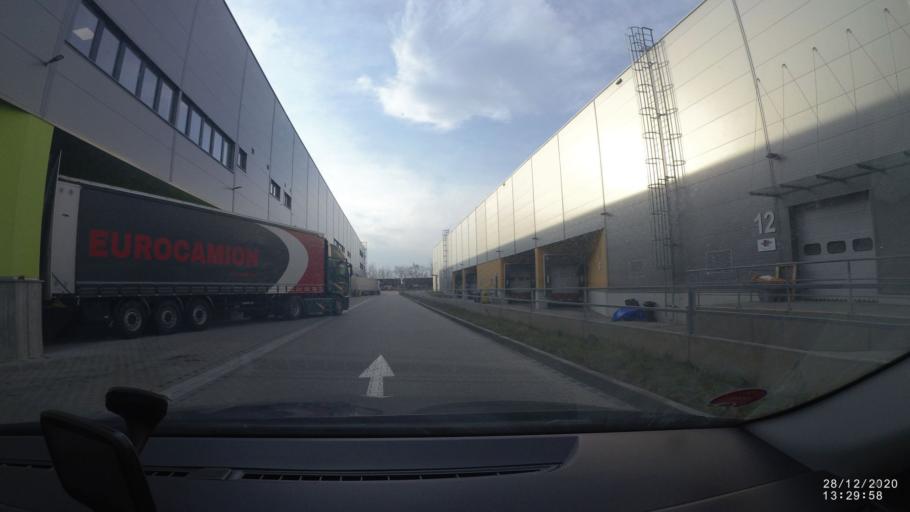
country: CZ
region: Central Bohemia
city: Jirny
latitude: 50.1256
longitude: 14.7121
